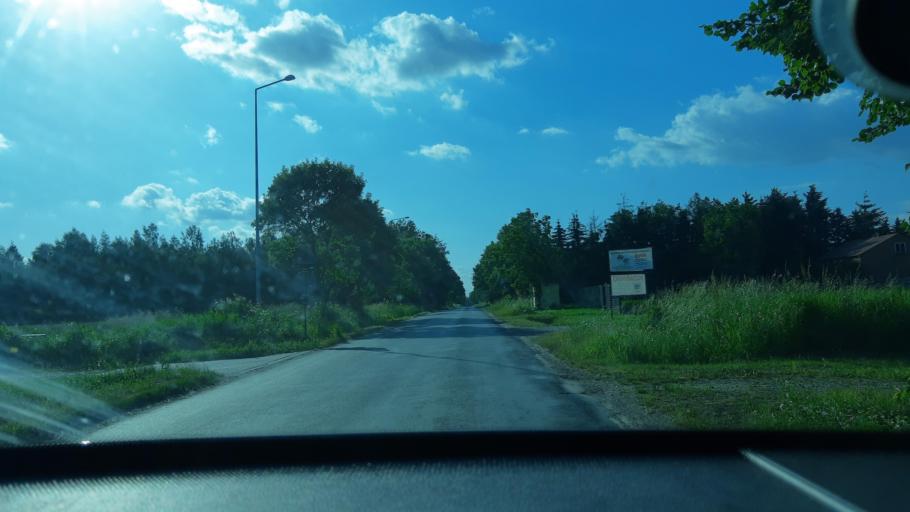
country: PL
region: Lodz Voivodeship
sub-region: Powiat sieradzki
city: Sieradz
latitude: 51.5509
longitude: 18.7701
